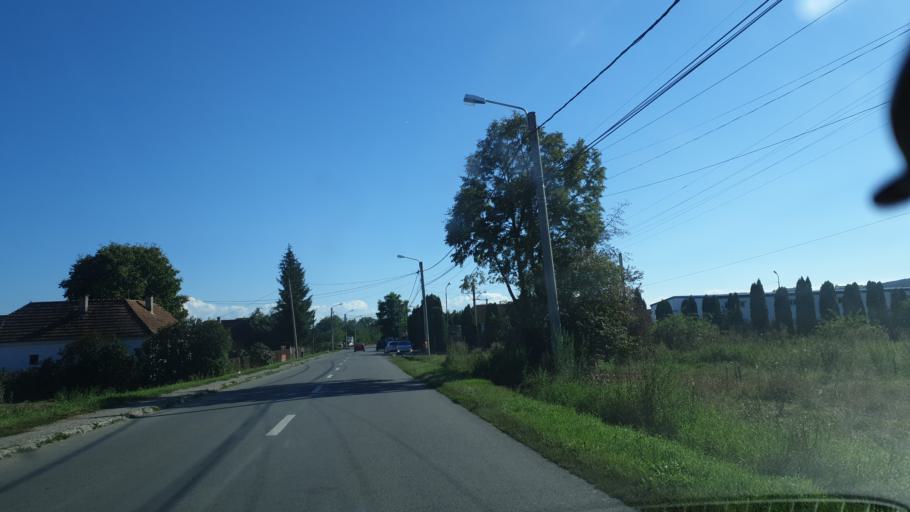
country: RO
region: Covasna
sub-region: Municipiul Sfantu Gheorghe
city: Sfantu-Gheorghe
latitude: 45.8496
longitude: 25.7776
